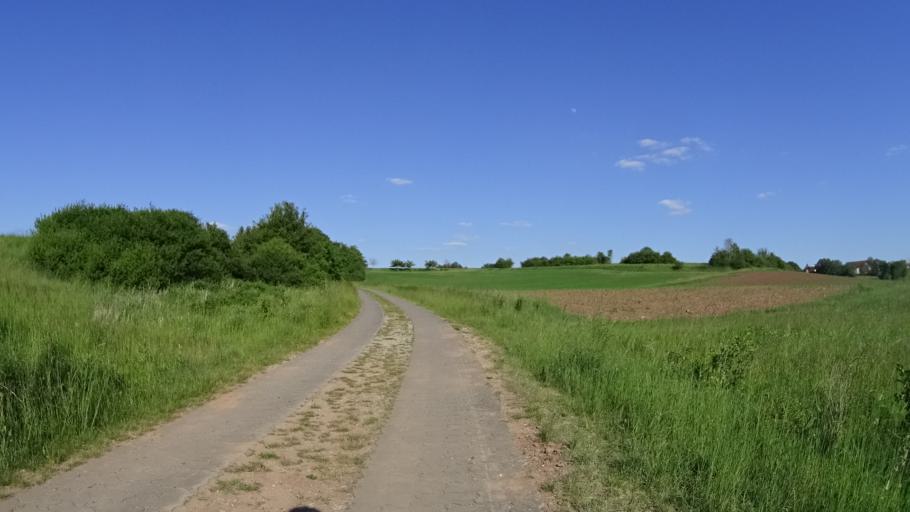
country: DE
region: Bavaria
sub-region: Regierungsbezirk Mittelfranken
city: Lichtenau
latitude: 49.1623
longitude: 10.3600
